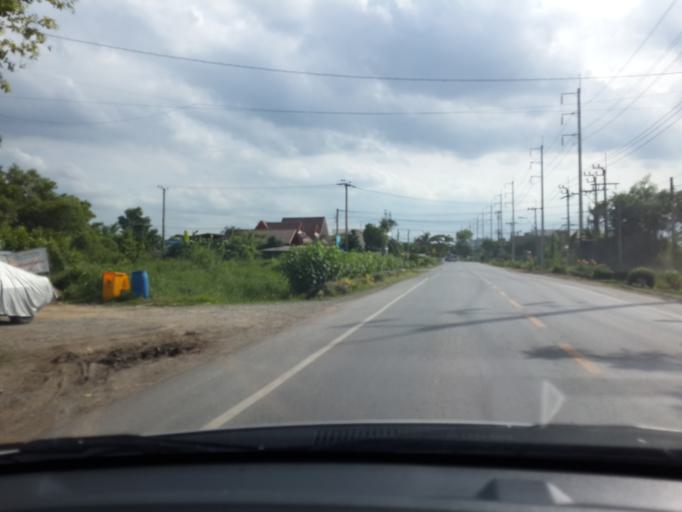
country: TH
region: Bangkok
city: Khlong Sam Wa
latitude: 13.8497
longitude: 100.7965
